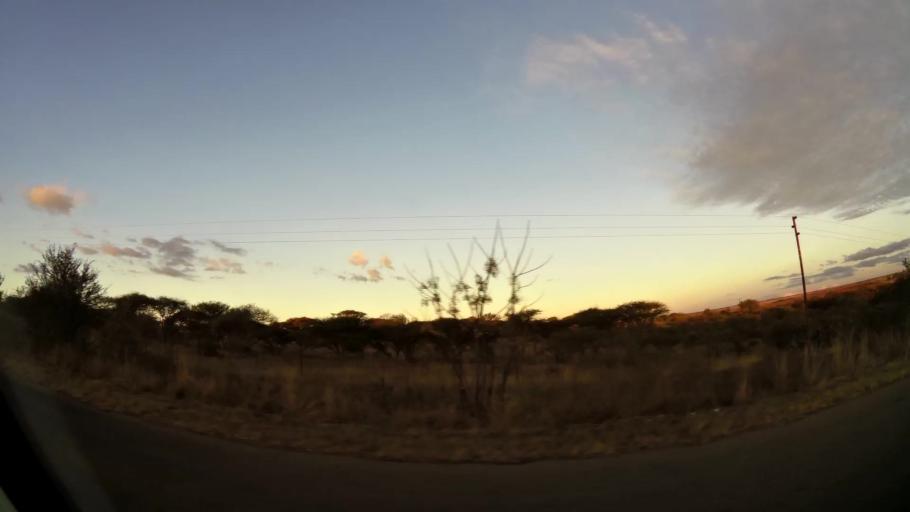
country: ZA
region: Limpopo
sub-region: Capricorn District Municipality
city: Polokwane
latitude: -23.7665
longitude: 29.4745
